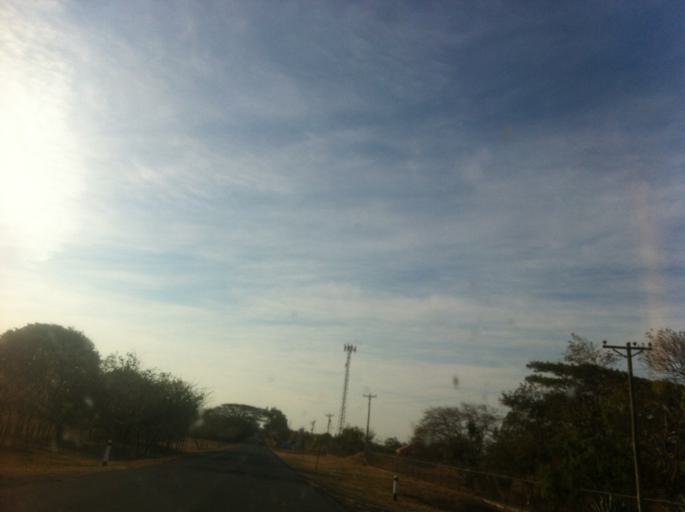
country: NI
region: Rivas
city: Rivas
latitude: 11.3481
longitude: -85.7372
